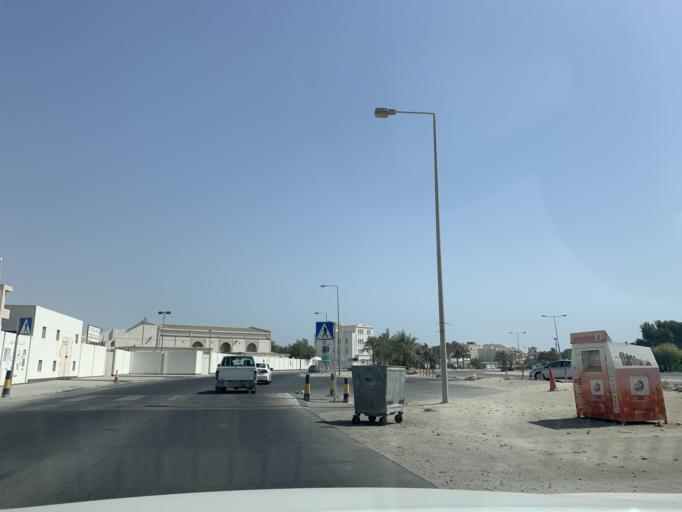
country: BH
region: Manama
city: Jidd Hafs
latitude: 26.2252
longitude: 50.4619
